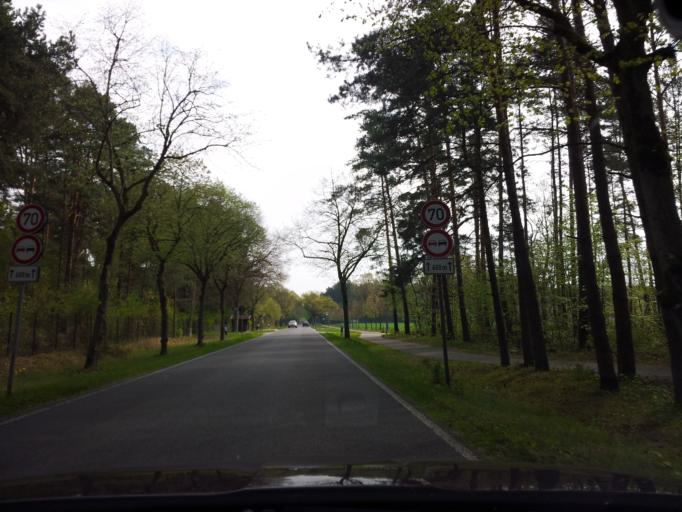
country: DE
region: Brandenburg
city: Rehfelde
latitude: 52.4547
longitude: 13.8926
